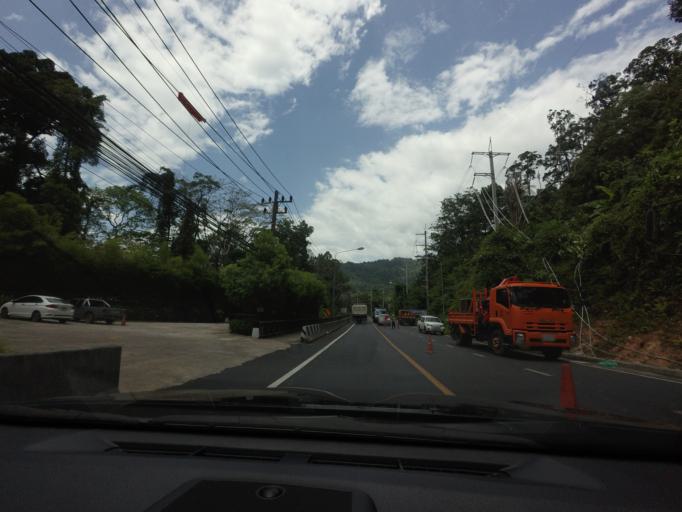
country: TH
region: Phangnga
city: Ban Khao Lak
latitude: 8.6356
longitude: 98.2464
